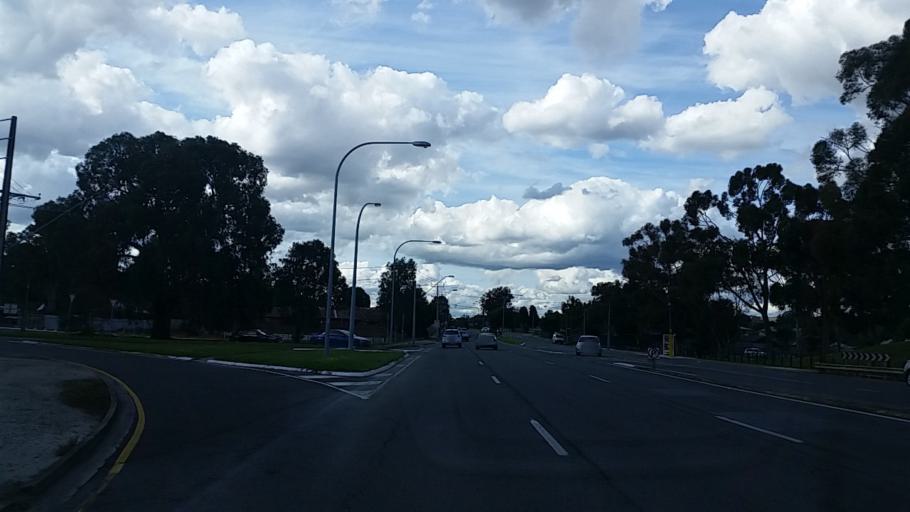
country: AU
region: South Australia
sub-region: Tea Tree Gully
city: Modbury
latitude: -34.8399
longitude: 138.6755
